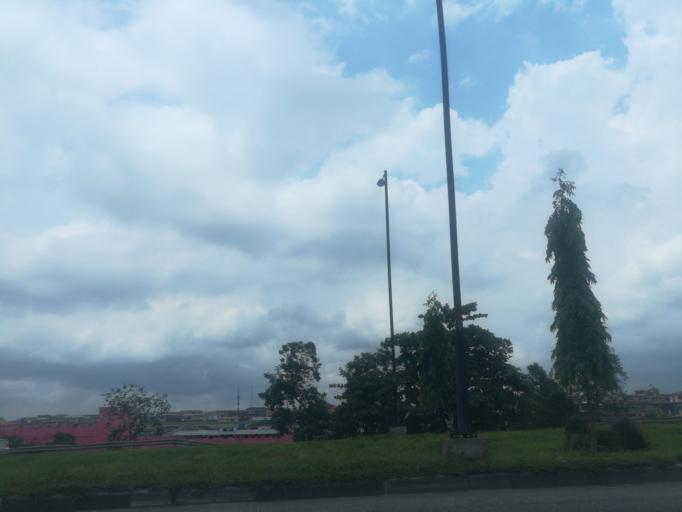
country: NG
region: Lagos
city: Ojota
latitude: 6.5897
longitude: 3.3861
